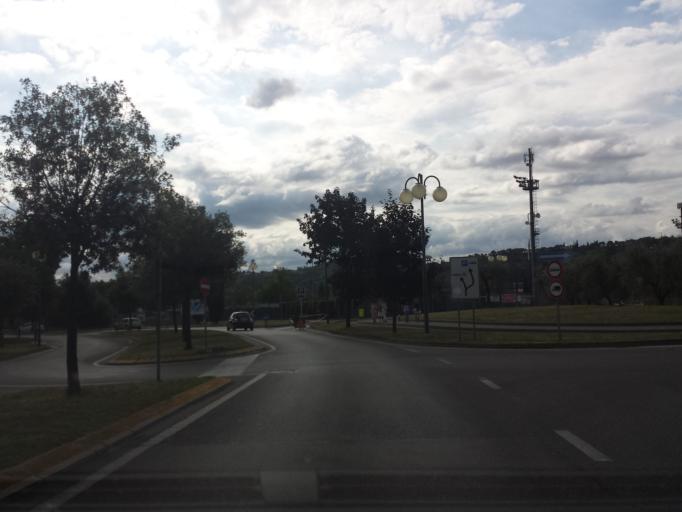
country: IT
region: Lombardy
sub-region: Provincia di Brescia
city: Salo
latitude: 45.6055
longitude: 10.5117
